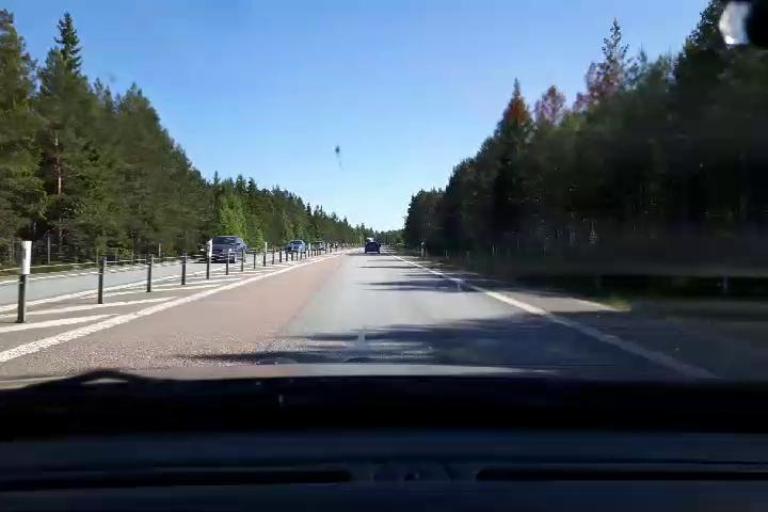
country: SE
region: Gaevleborg
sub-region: Gavle Kommun
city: Norrsundet
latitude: 60.8498
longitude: 17.0717
